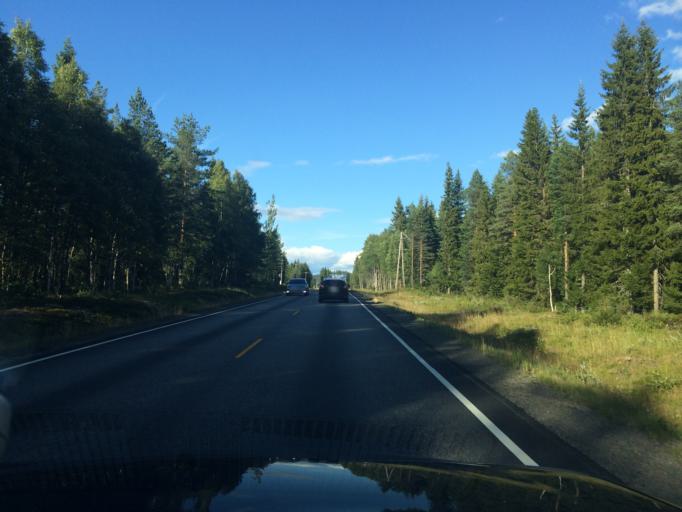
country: NO
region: Hedmark
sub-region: Elverum
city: Elverum
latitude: 61.0143
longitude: 11.8396
